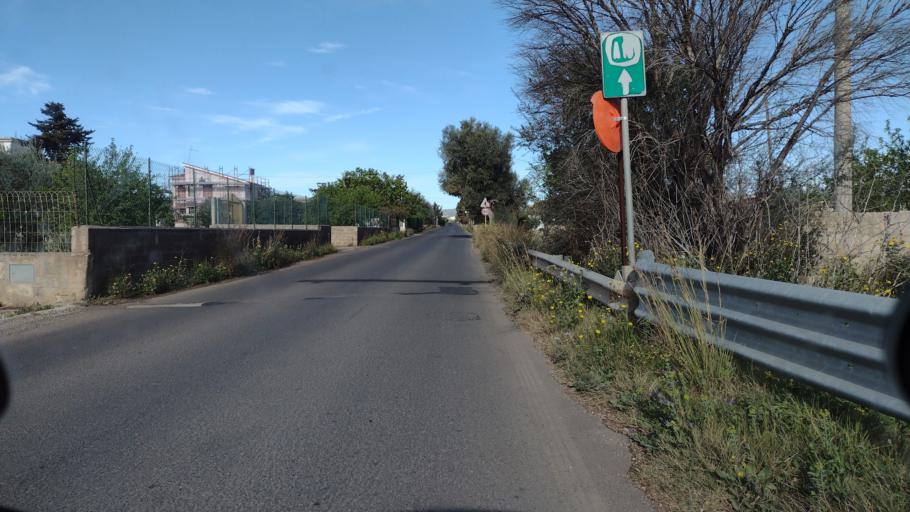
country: IT
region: Sicily
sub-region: Provincia di Siracusa
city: Avola
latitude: 36.8743
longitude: 15.1150
